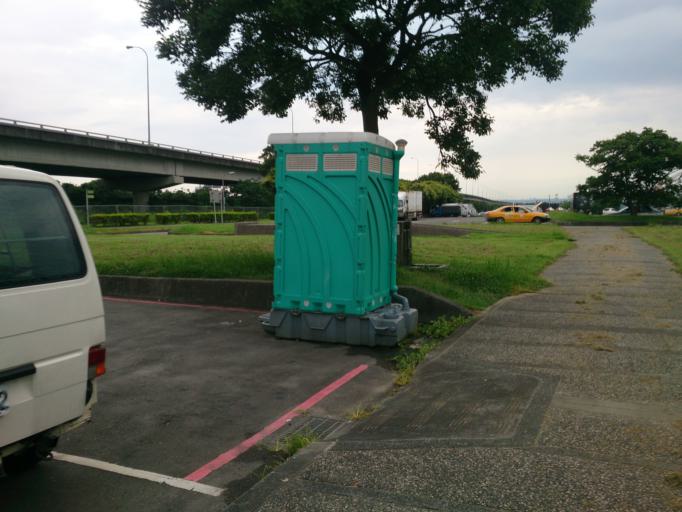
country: TW
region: Taipei
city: Taipei
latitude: 25.0737
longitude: 121.5556
